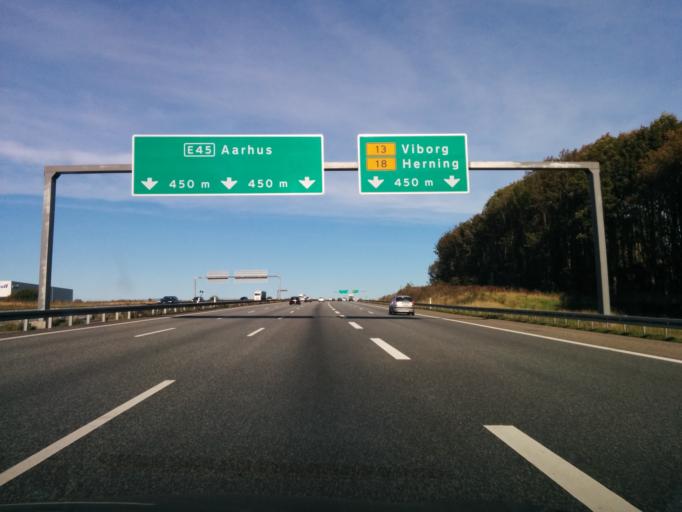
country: DK
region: South Denmark
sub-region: Vejle Kommune
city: Vejle
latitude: 55.7317
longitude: 9.5766
